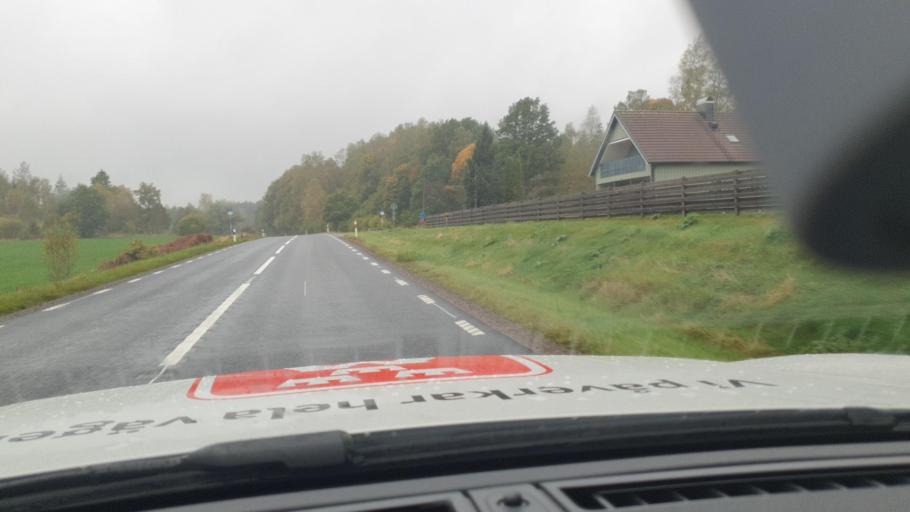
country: SE
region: Vaestra Goetaland
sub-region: Marks Kommun
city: Horred
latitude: 57.1570
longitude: 12.7363
